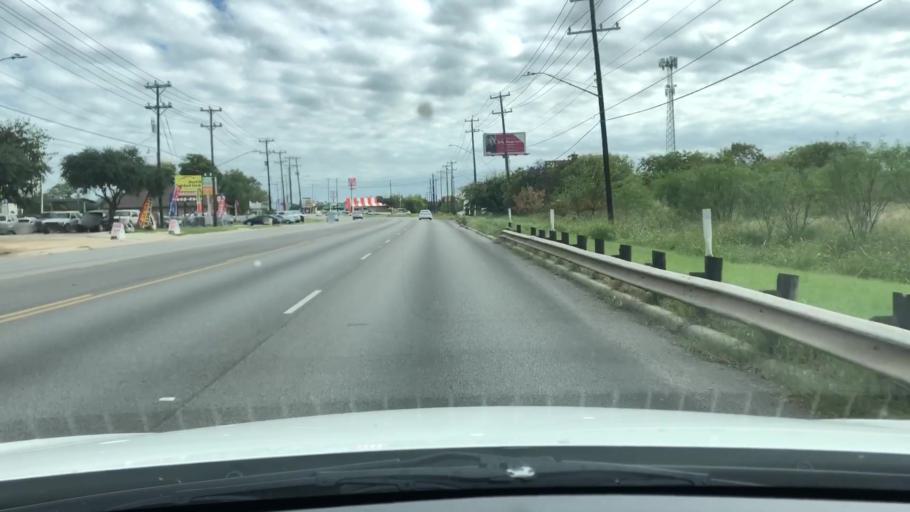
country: US
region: Texas
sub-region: Bexar County
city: Leon Valley
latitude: 29.4816
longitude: -98.6610
